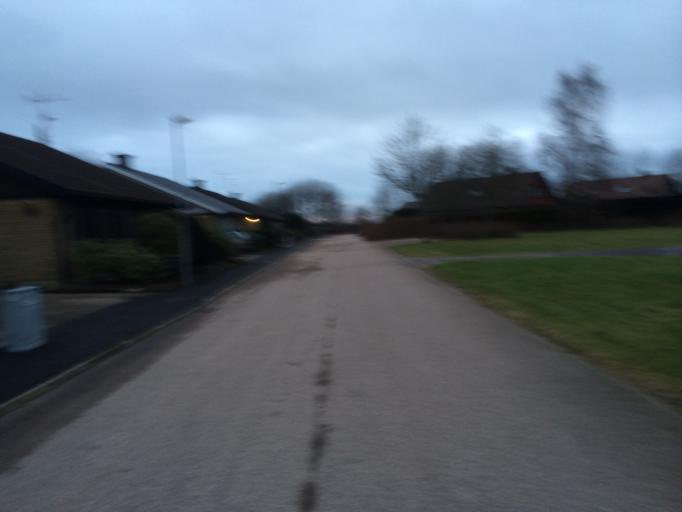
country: SE
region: Halland
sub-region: Halmstads Kommun
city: Halmstad
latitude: 56.6783
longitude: 12.8277
